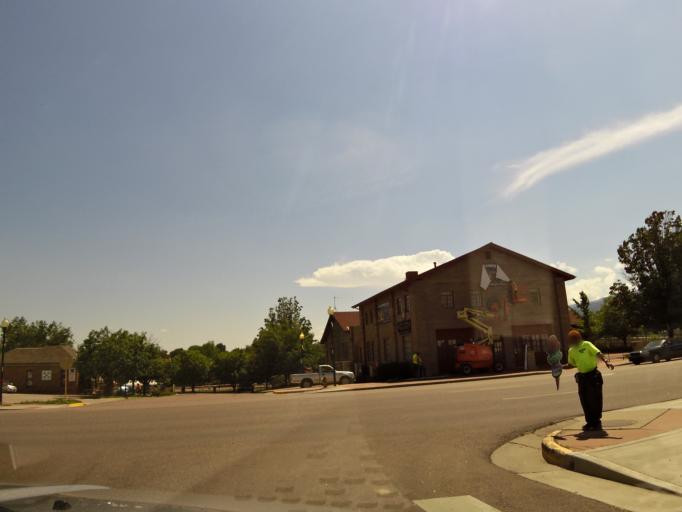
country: US
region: Colorado
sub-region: Fremont County
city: Canon City
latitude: 38.4392
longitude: -105.2415
